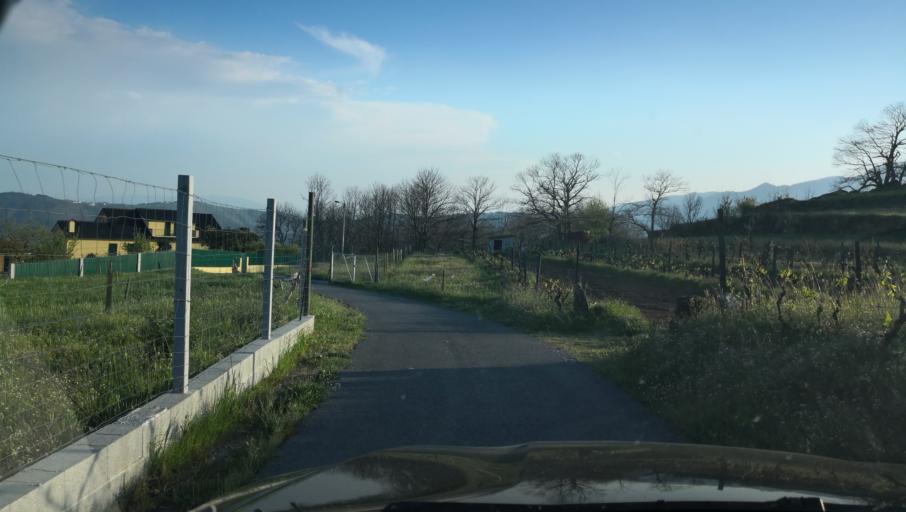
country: PT
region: Vila Real
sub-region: Santa Marta de Penaguiao
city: Santa Marta de Penaguiao
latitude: 41.2641
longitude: -7.8113
